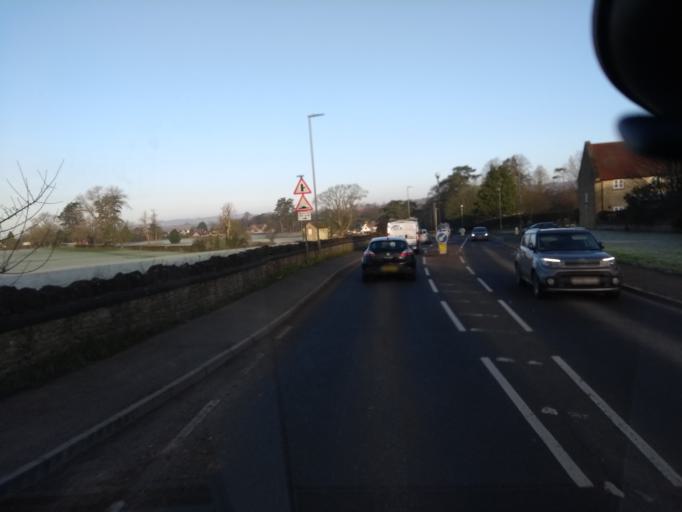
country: GB
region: England
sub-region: Somerset
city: Shepton Mallet
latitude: 51.1824
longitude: -2.5414
